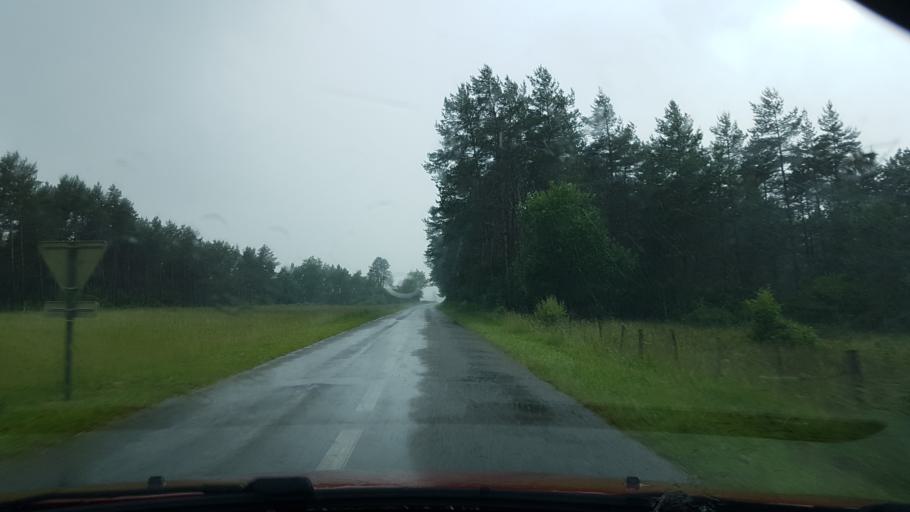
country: FR
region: Franche-Comte
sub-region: Departement du Jura
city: Clairvaux-les-Lacs
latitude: 46.5586
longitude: 5.7250
